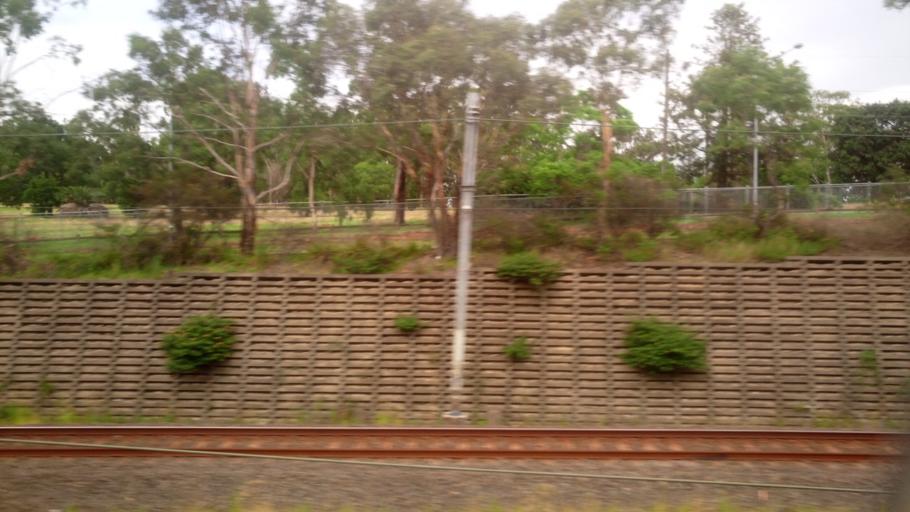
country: AU
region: New South Wales
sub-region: Parramatta
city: City of Parramatta
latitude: -33.8135
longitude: 150.9955
